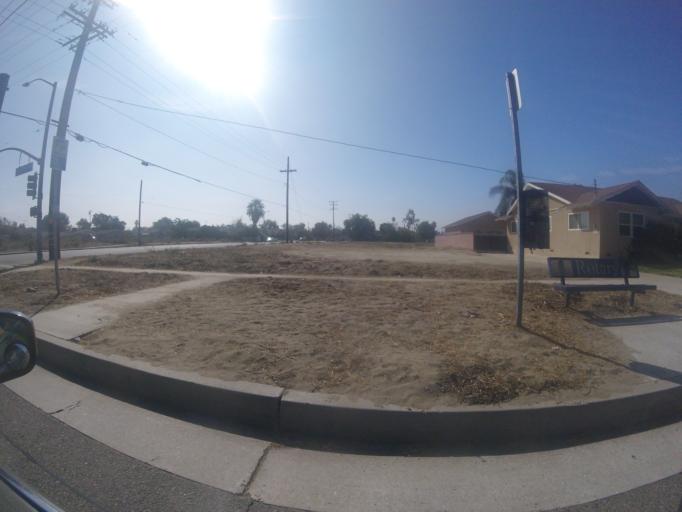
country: US
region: California
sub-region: San Bernardino County
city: Lake Arrowhead
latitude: 34.2056
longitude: -117.2252
